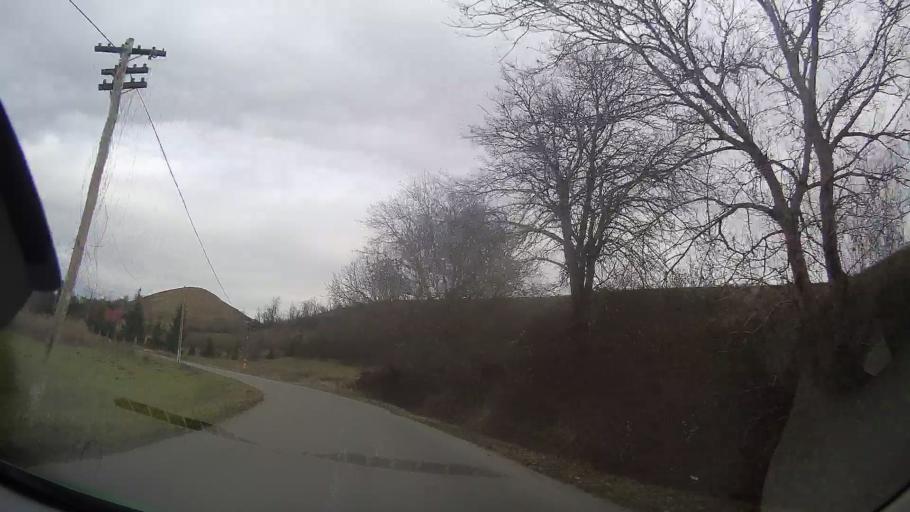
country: RO
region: Mures
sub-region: Comuna Faragau
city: Faragau
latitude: 46.7378
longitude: 24.5404
